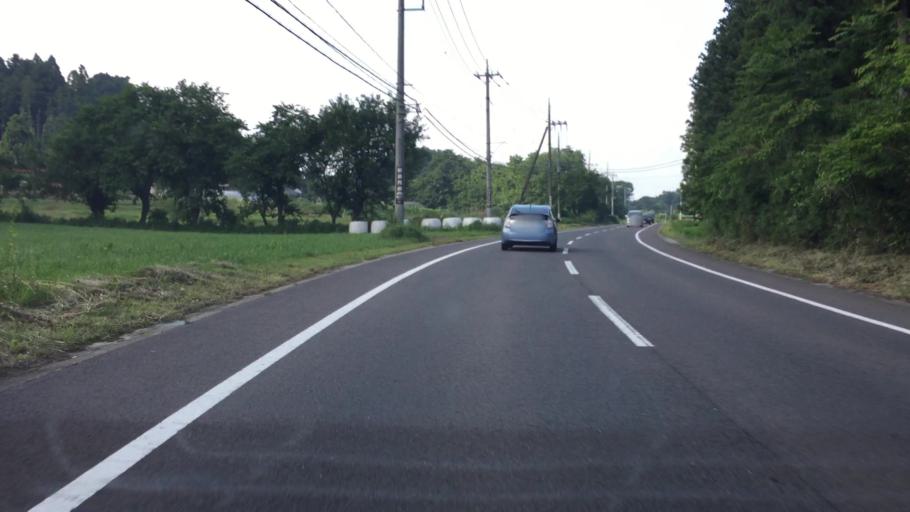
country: JP
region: Tochigi
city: Kuroiso
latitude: 37.0754
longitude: 140.0485
